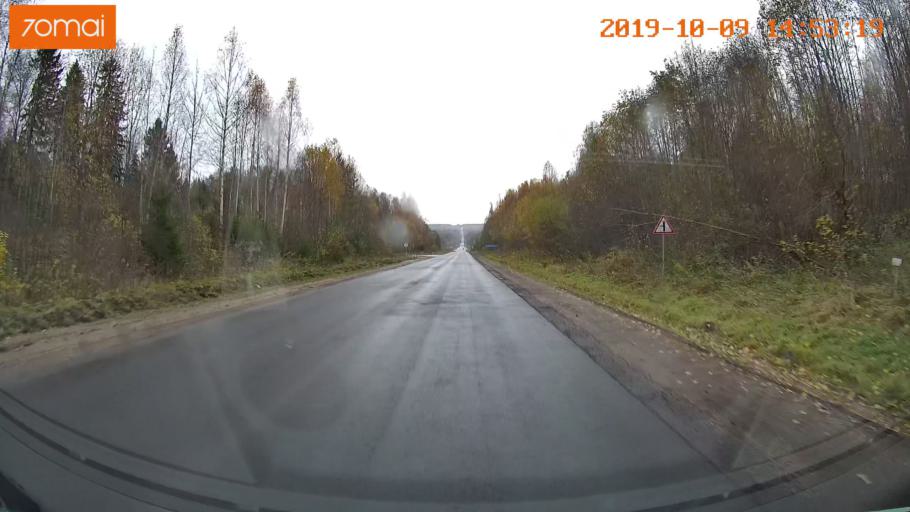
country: RU
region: Kostroma
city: Chistyye Bory
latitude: 58.3691
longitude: 41.6377
